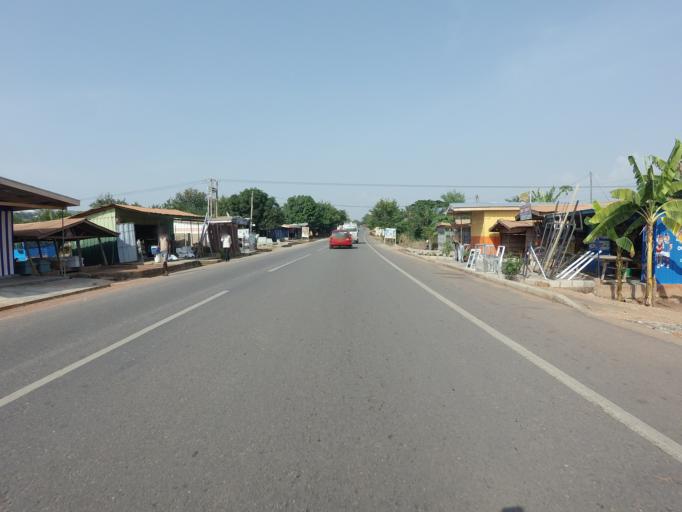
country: GH
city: Akropong
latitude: 6.1245
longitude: -0.0015
